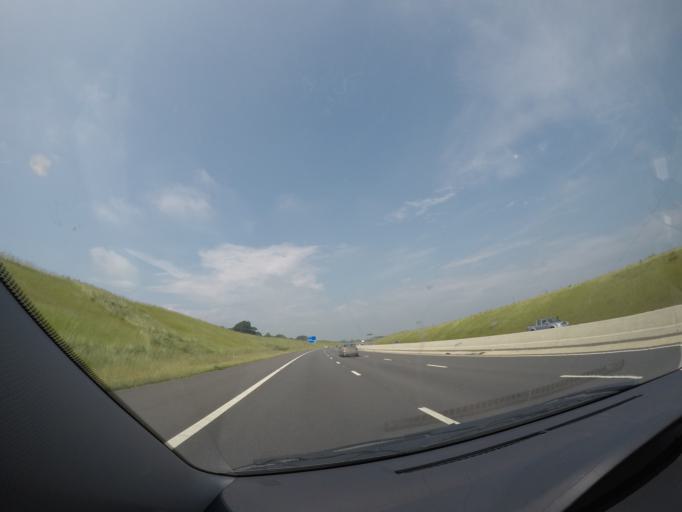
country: GB
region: England
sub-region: North Yorkshire
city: Catterick
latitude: 54.3627
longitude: -1.6278
